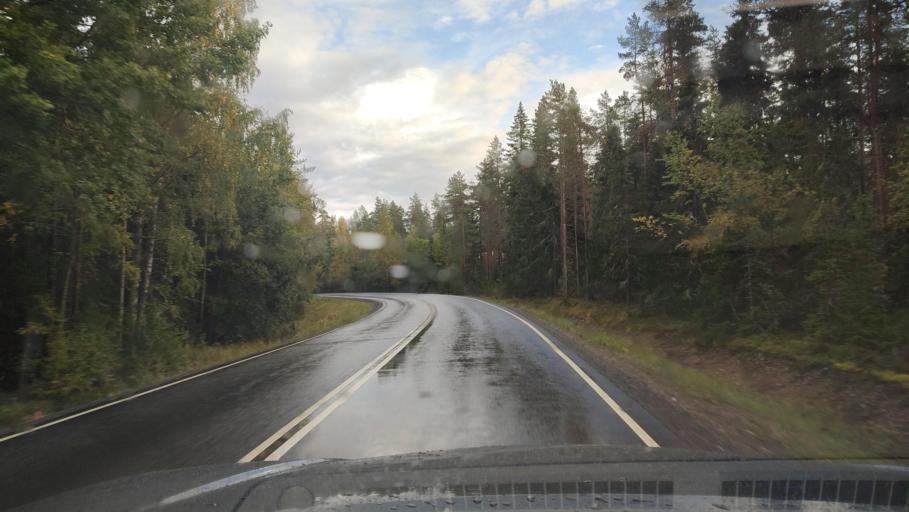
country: FI
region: Southern Ostrobothnia
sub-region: Suupohja
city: Karijoki
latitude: 62.2916
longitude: 21.6447
